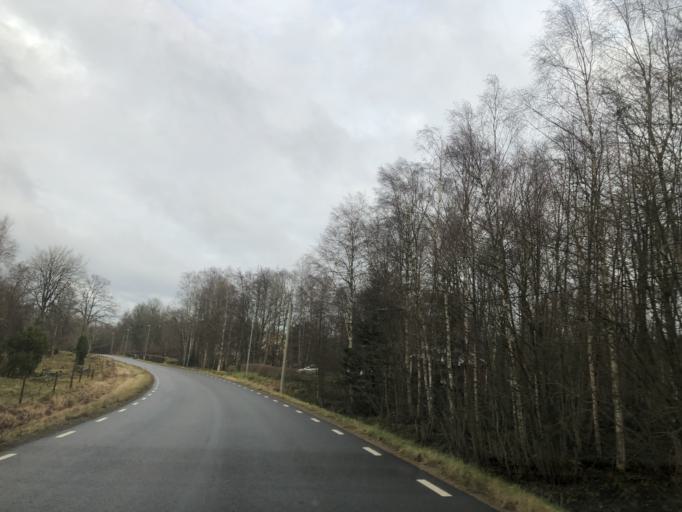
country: SE
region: Vaestra Goetaland
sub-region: Ulricehamns Kommun
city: Ulricehamn
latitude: 57.8304
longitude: 13.2562
